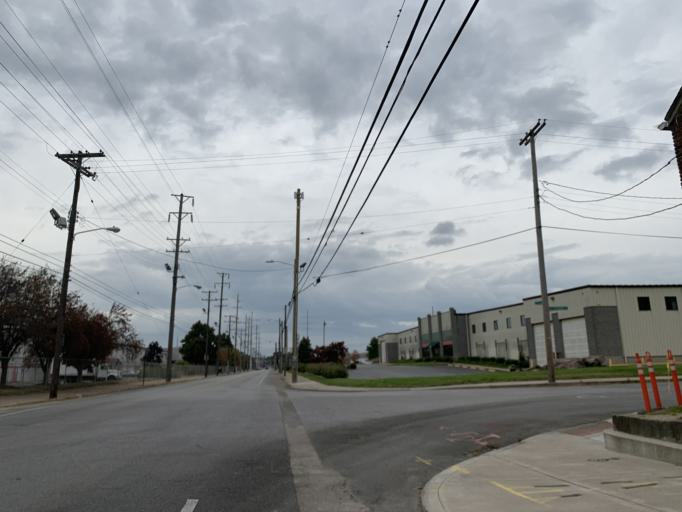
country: US
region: Kentucky
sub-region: Jefferson County
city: Louisville
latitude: 38.2384
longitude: -85.7732
